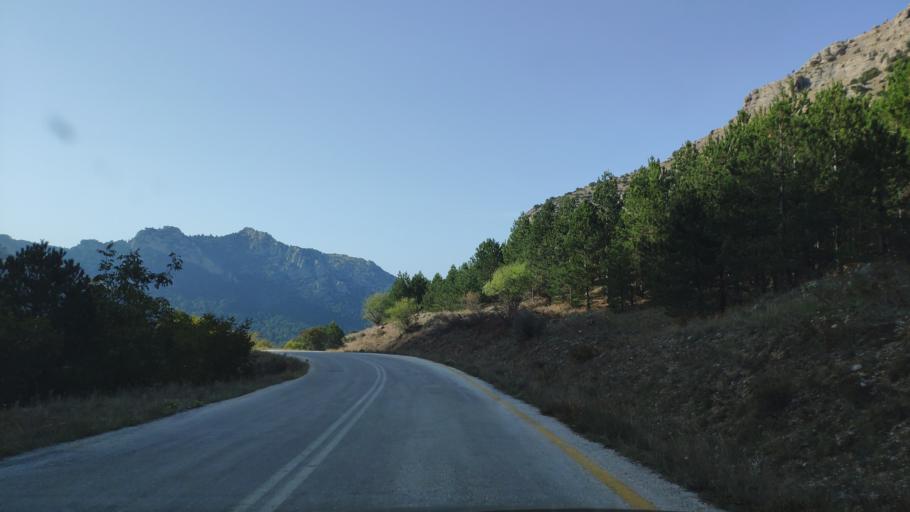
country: GR
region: West Greece
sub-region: Nomos Achaias
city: Aiyira
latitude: 38.0415
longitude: 22.3929
